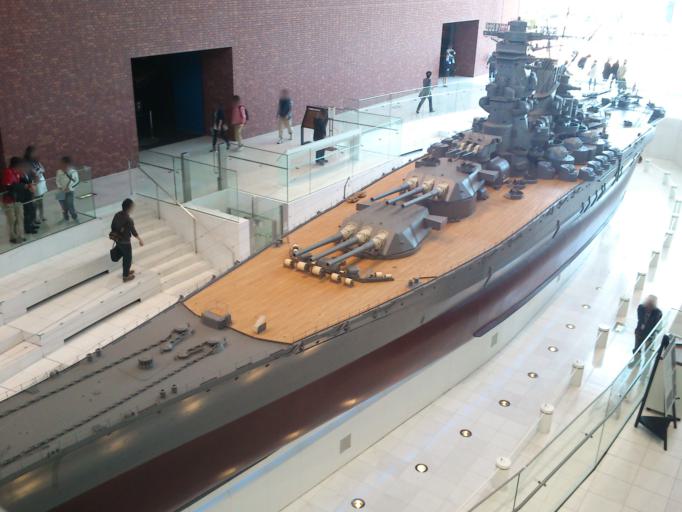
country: JP
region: Hiroshima
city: Kure
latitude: 34.2410
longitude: 132.5563
